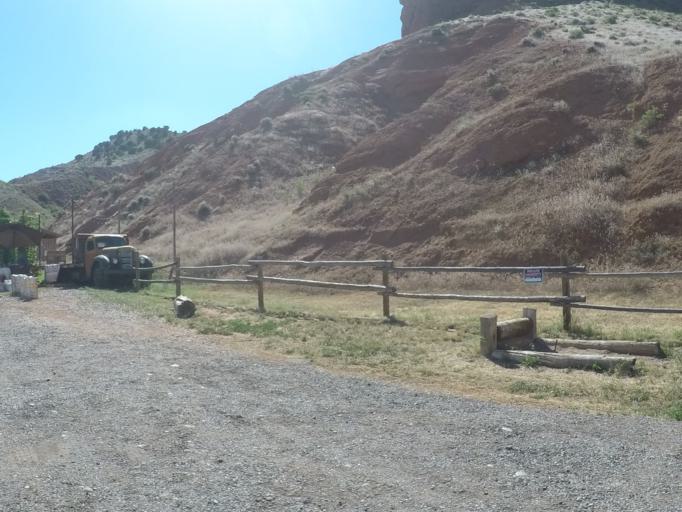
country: US
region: Wyoming
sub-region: Washakie County
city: Worland
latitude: 44.0301
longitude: -107.4690
